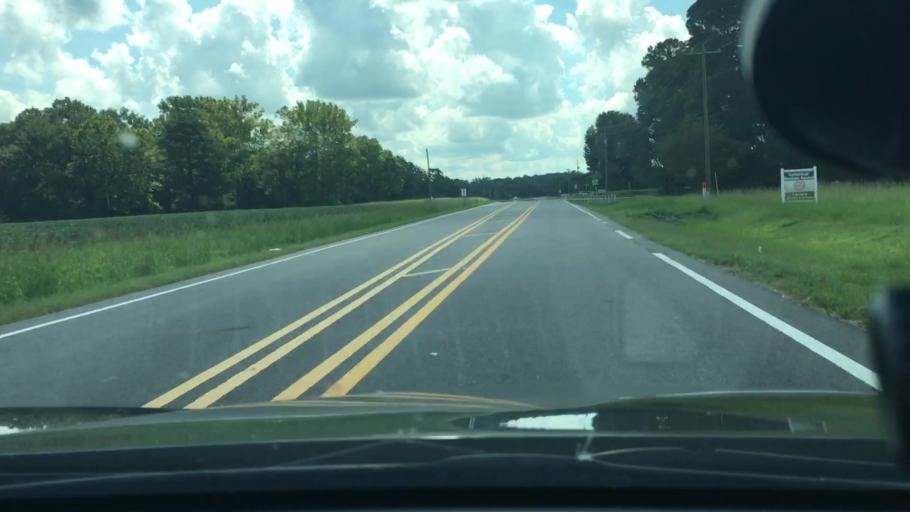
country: US
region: North Carolina
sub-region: Pitt County
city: Summerfield
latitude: 35.6500
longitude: -77.4638
